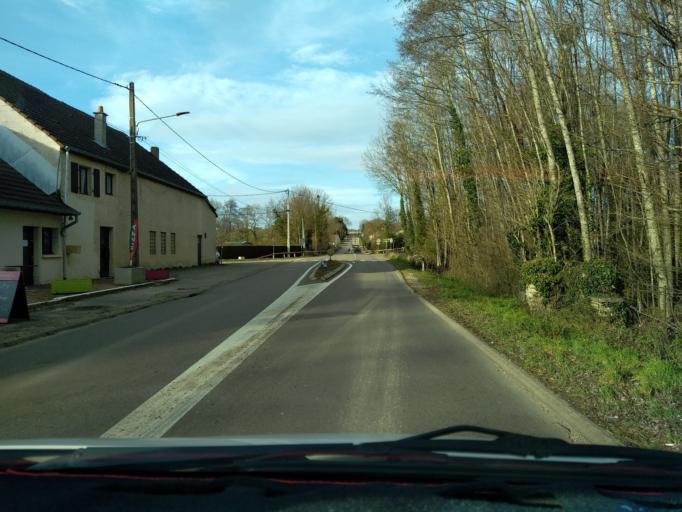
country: FR
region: Franche-Comte
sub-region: Departement de la Haute-Saone
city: Gray
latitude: 47.3904
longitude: 5.6532
